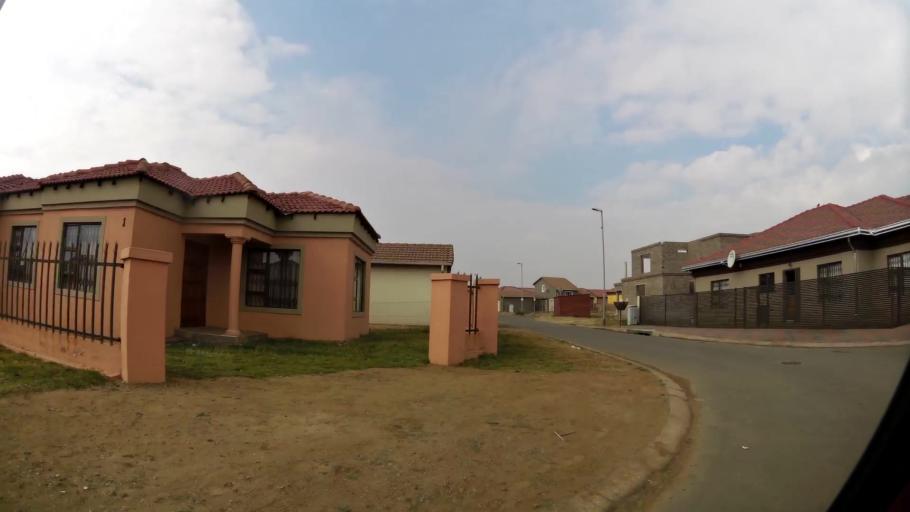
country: ZA
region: Gauteng
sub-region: Sedibeng District Municipality
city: Vanderbijlpark
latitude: -26.6843
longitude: 27.8500
